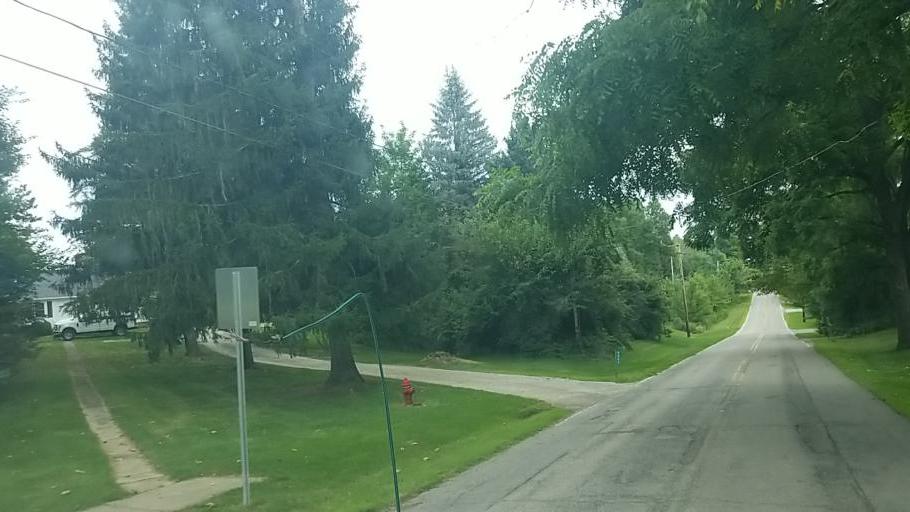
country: US
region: Ohio
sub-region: Medina County
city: Westfield Center
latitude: 41.0201
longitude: -81.9329
